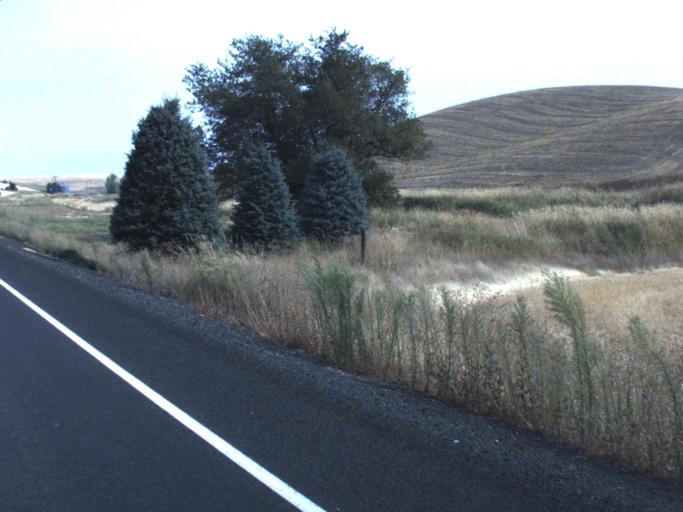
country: US
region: Washington
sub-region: Whitman County
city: Pullman
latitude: 46.8079
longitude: -117.1231
